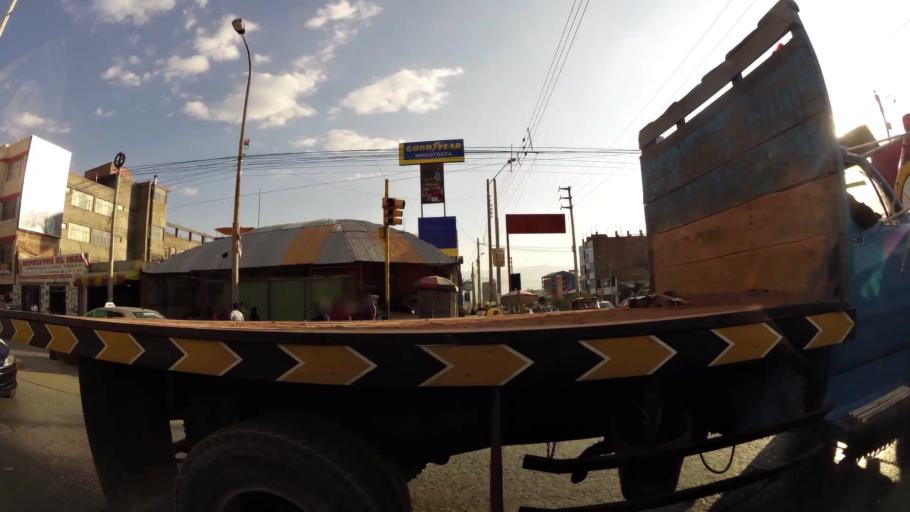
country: PE
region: Junin
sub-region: Provincia de Huancayo
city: El Tambo
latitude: -12.0543
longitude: -75.2191
